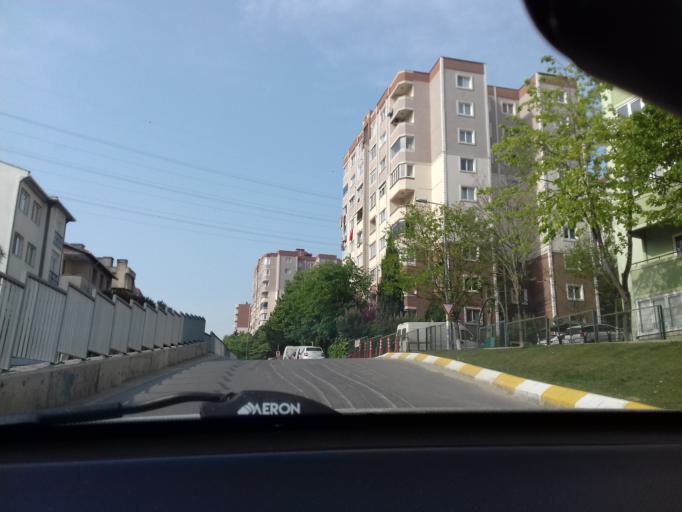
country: TR
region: Istanbul
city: Pendik
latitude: 40.9105
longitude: 29.2823
